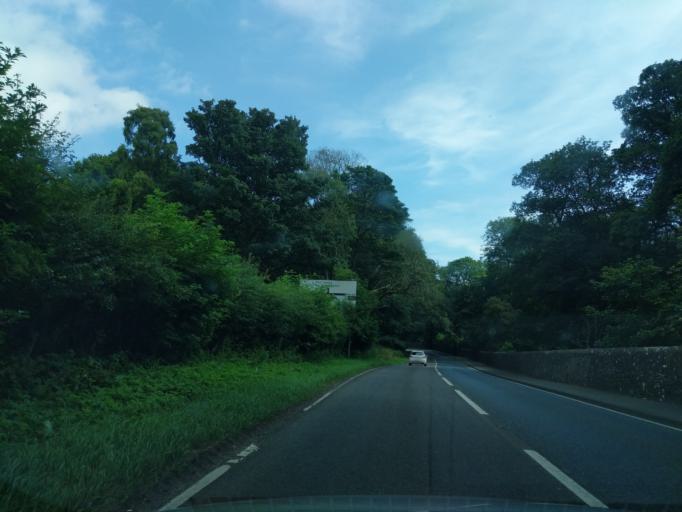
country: GB
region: Scotland
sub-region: Angus
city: Muirhead
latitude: 56.4842
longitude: -3.0265
